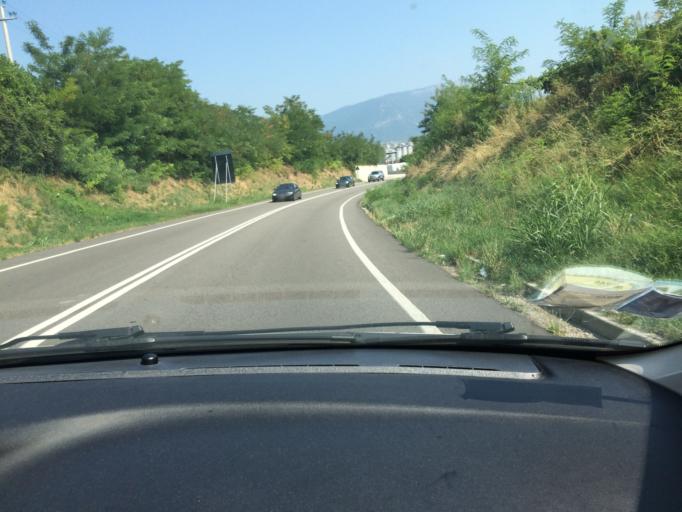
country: IT
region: Veneto
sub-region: Provincia di Verona
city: Cavajon Veronese
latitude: 45.5445
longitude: 10.7749
